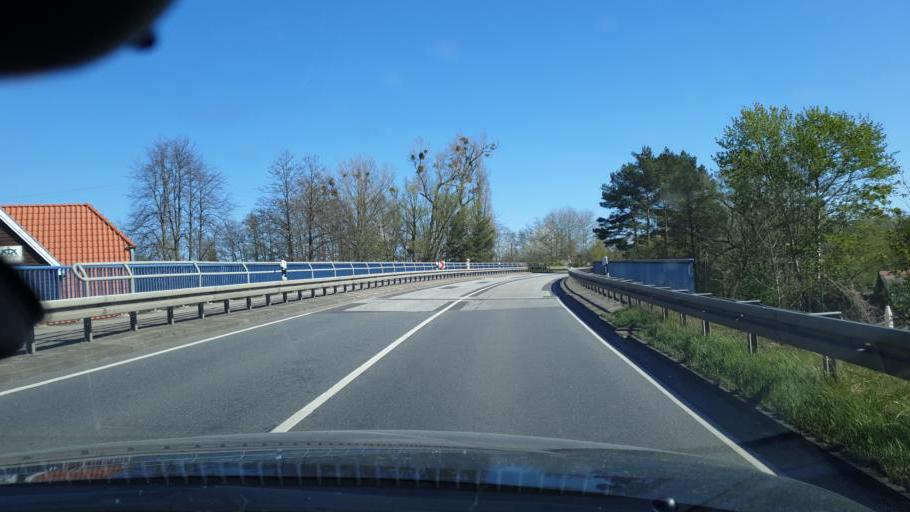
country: DE
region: Mecklenburg-Vorpommern
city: Seehof
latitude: 53.6778
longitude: 11.4501
